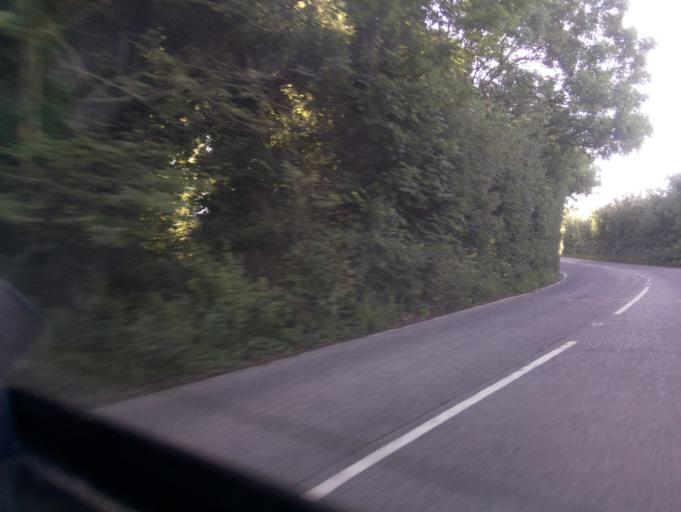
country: GB
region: England
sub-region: South Gloucestershire
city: Pucklechurch
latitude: 51.4426
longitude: -2.4152
